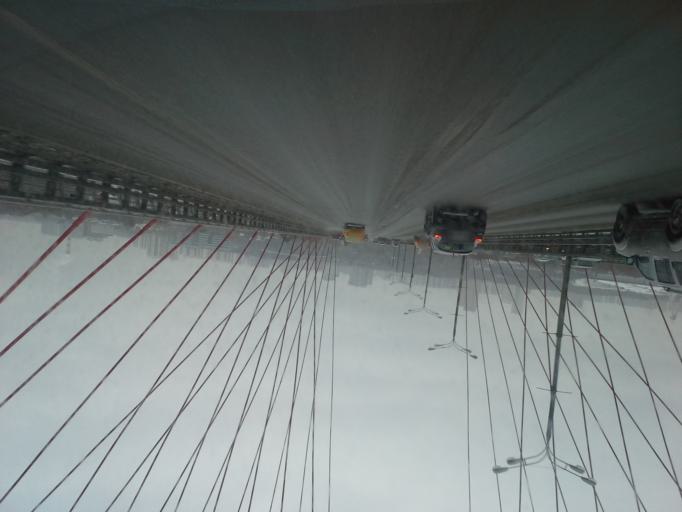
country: RU
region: Moscow
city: Shchukino
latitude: 55.7766
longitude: 37.4436
